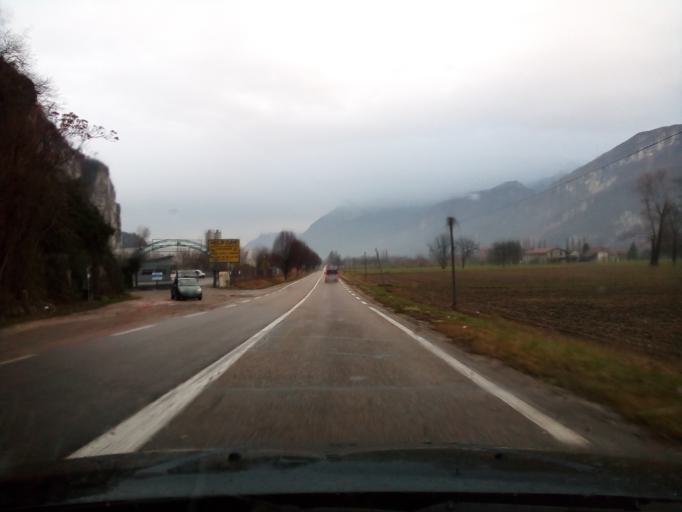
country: FR
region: Rhone-Alpes
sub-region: Departement de l'Isere
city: La Buisse
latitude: 45.3159
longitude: 5.6221
